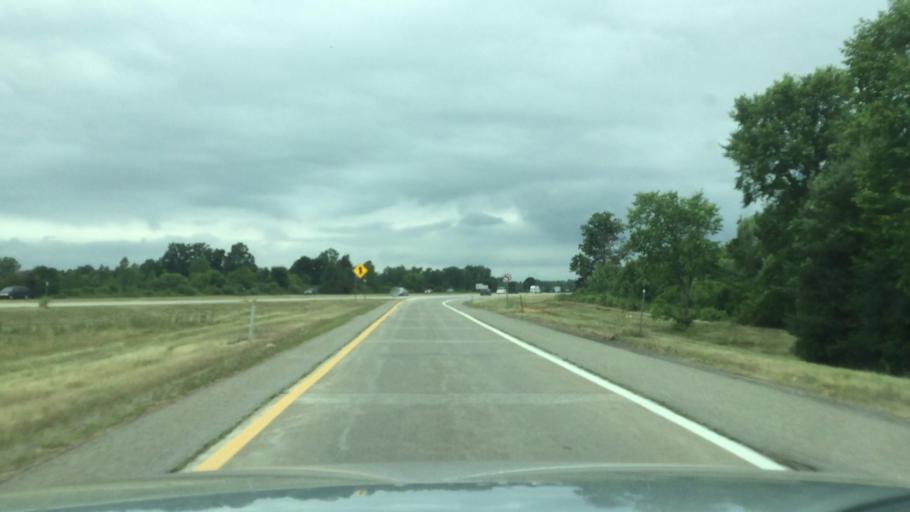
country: US
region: Michigan
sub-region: Genesee County
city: Davison
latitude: 43.0120
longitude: -83.5224
